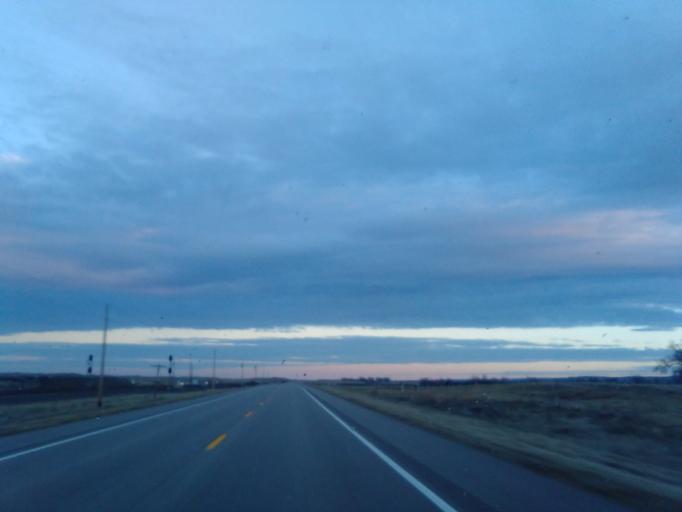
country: US
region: Nebraska
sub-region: Garden County
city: Oshkosh
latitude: 41.3869
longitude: -102.2883
